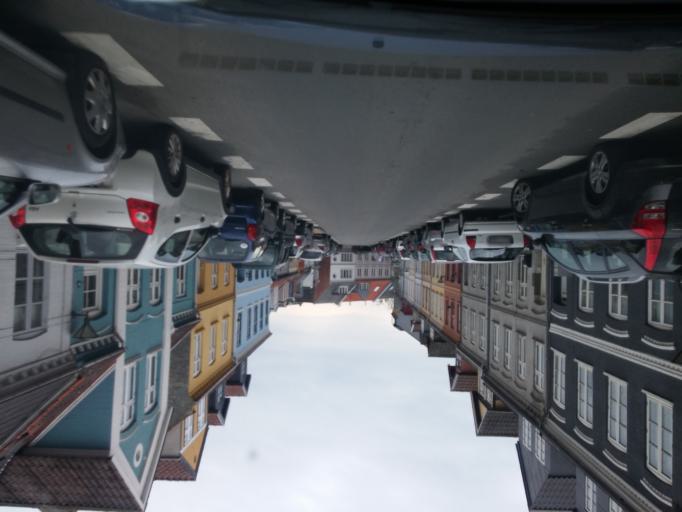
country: DK
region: South Denmark
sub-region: Odense Kommune
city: Odense
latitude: 55.3957
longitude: 10.3764
